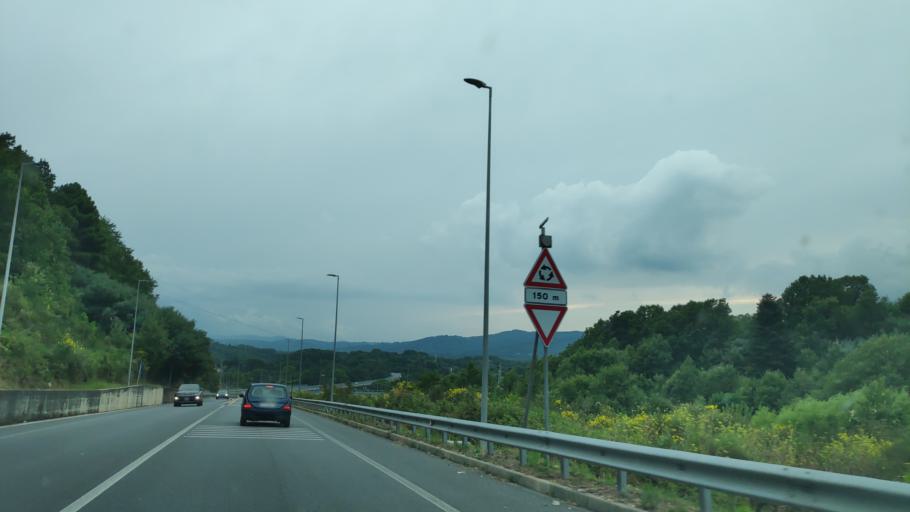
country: IT
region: Calabria
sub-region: Provincia di Catanzaro
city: Chiaravalle Centrale
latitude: 38.6759
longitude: 16.4146
